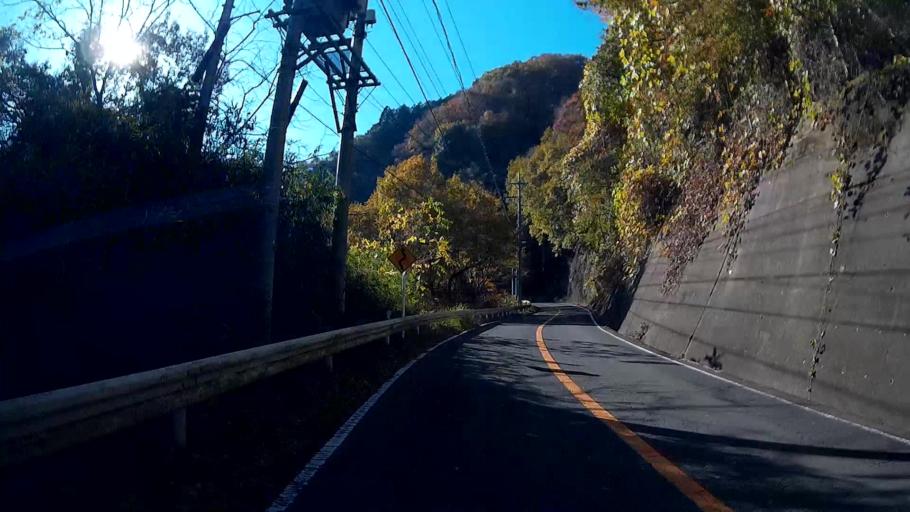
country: JP
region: Yamanashi
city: Uenohara
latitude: 35.6060
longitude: 139.1235
